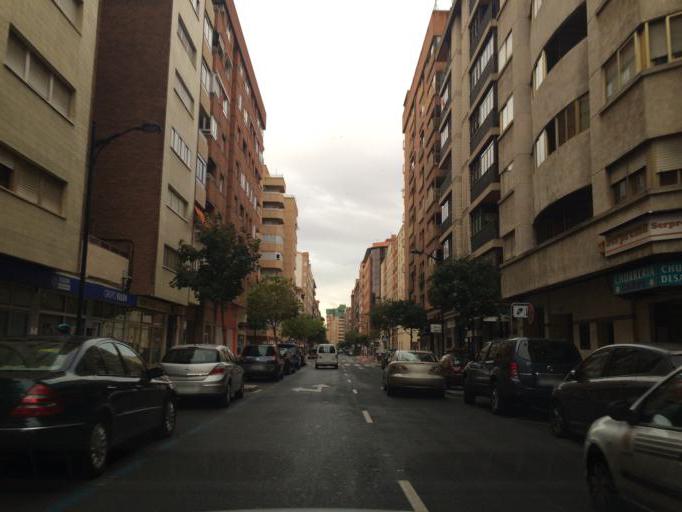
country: ES
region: Castille-La Mancha
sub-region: Provincia de Albacete
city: Albacete
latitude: 39.0000
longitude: -1.8596
